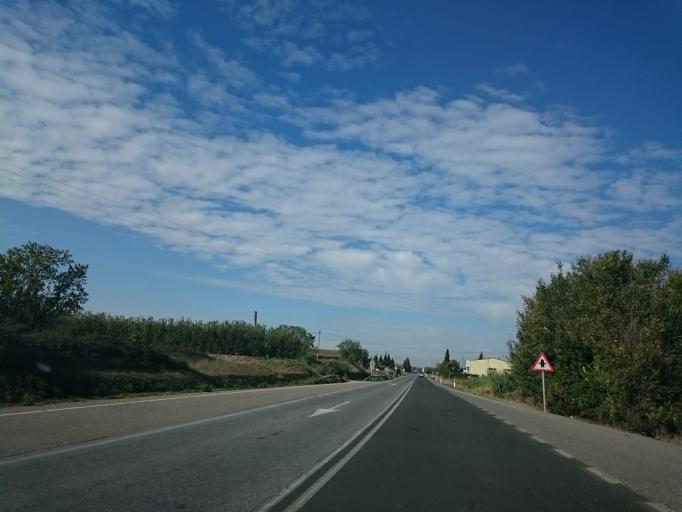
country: ES
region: Catalonia
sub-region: Provincia de Lleida
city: Juneda
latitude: 41.5406
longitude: 0.8288
